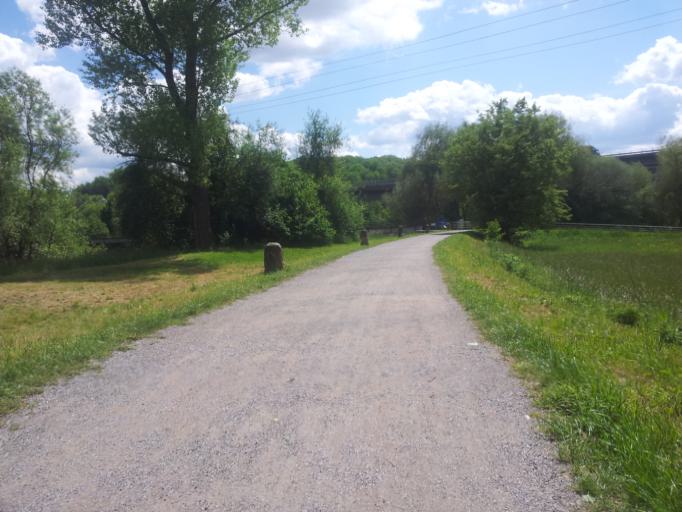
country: DE
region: Baden-Wuerttemberg
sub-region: Regierungsbezirk Stuttgart
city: Plochingen
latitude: 48.7051
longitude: 9.4195
